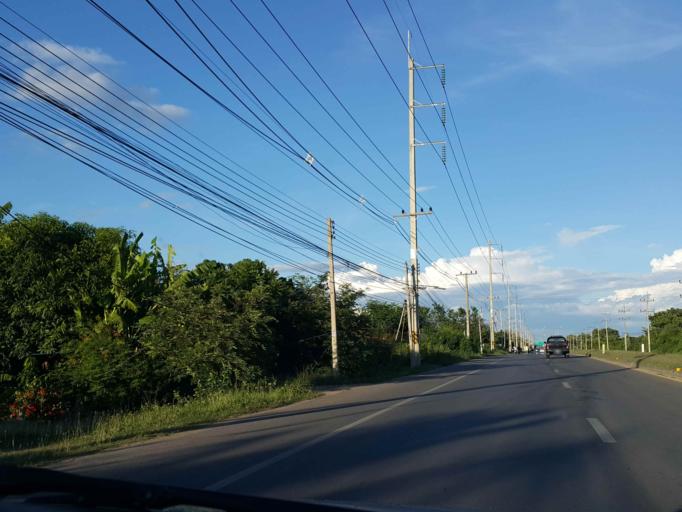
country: TH
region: Lamphun
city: Wiang Nong Long
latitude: 18.4515
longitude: 98.7373
